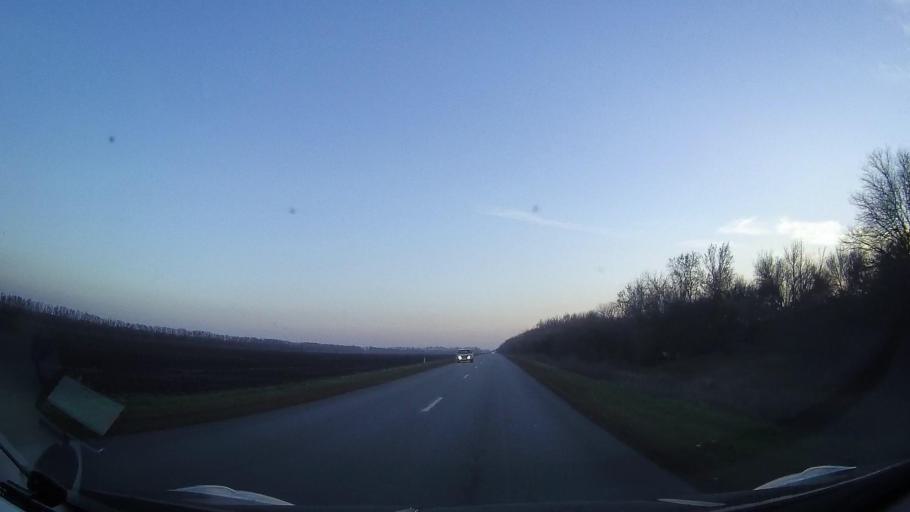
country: RU
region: Rostov
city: Zernograd
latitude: 47.0230
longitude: 40.3917
